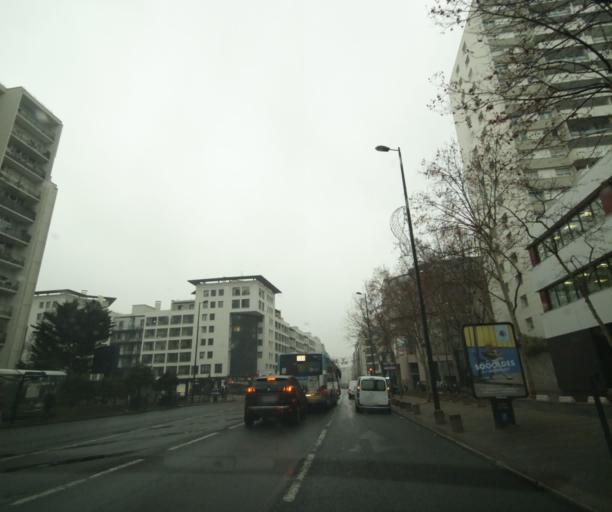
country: FR
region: Ile-de-France
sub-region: Departement des Hauts-de-Seine
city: Levallois-Perret
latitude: 48.8931
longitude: 2.3001
